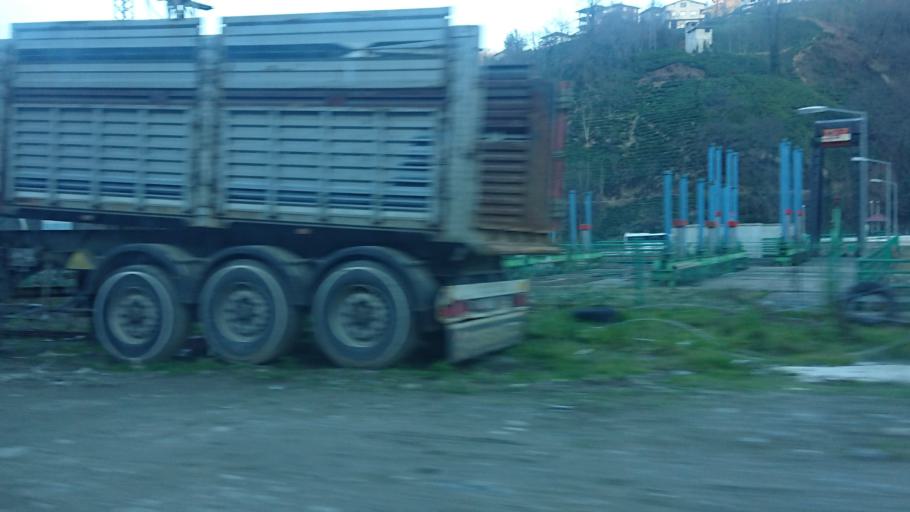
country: TR
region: Rize
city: Gundogdu
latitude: 41.0219
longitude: 40.5763
